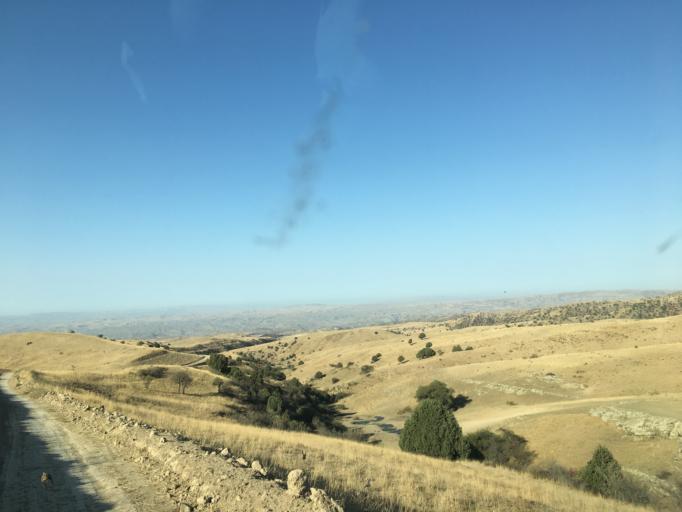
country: TM
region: Ahal
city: Baharly
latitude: 38.3290
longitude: 56.8829
